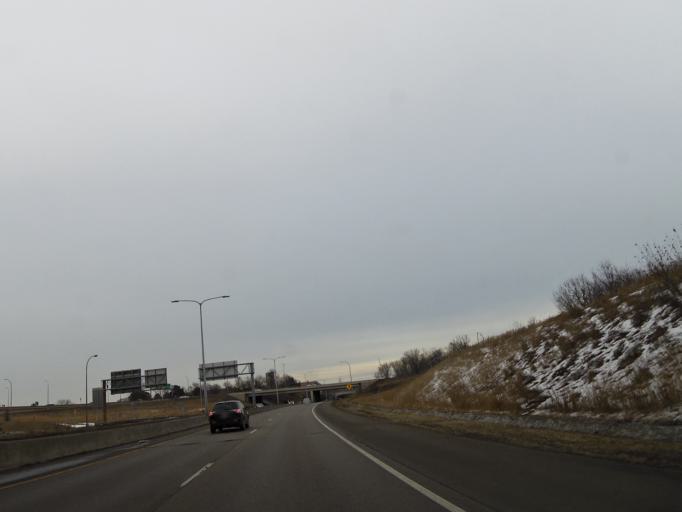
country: US
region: Minnesota
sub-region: Dakota County
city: Mendota Heights
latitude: 44.8895
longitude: -93.1862
